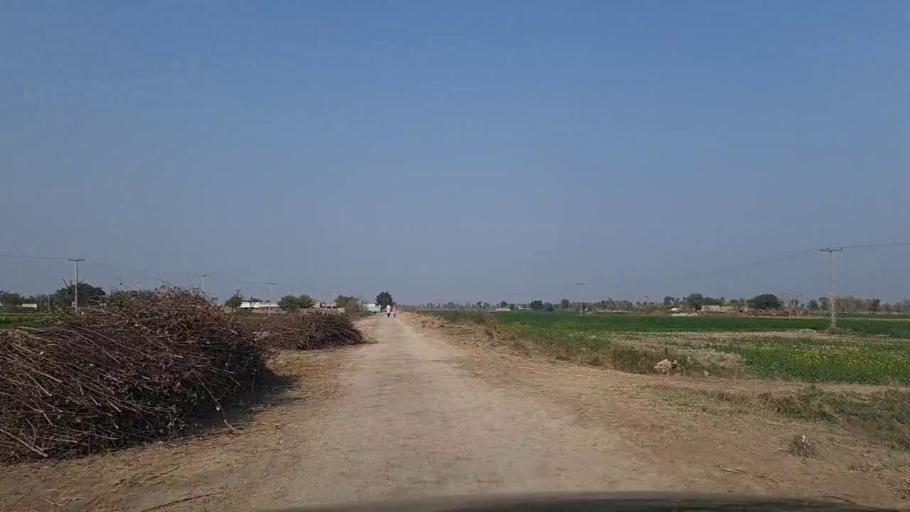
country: PK
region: Sindh
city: Daur
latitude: 26.4081
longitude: 68.4188
